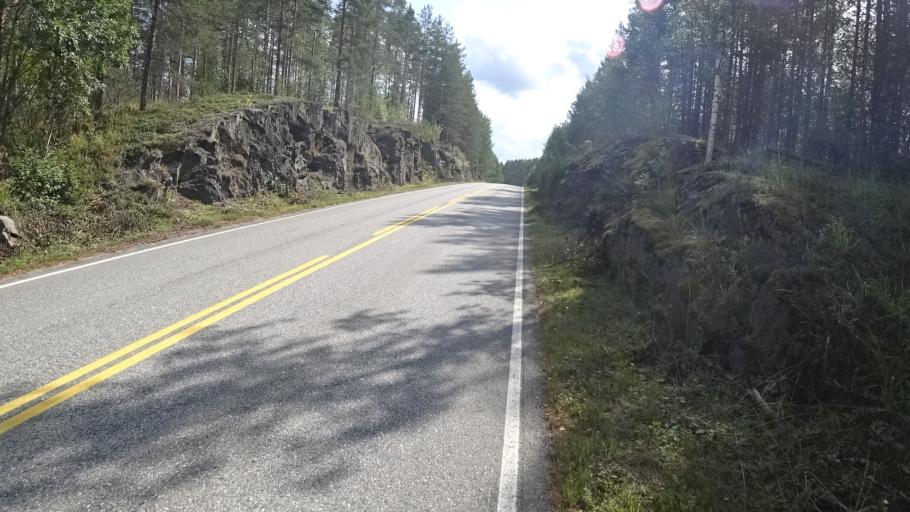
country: FI
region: North Karelia
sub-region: Joensuu
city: Ilomantsi
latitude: 62.6205
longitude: 31.2001
